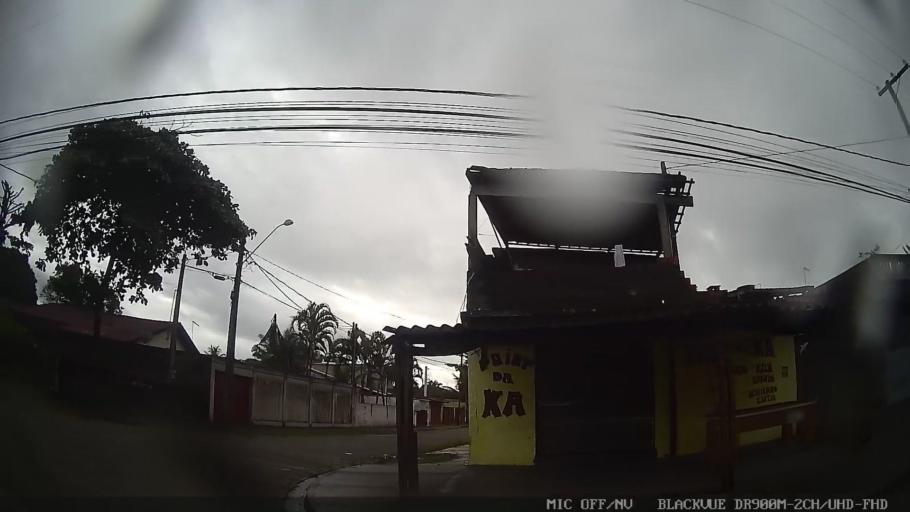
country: BR
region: Sao Paulo
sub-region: Itanhaem
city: Itanhaem
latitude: -24.2336
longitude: -46.8838
